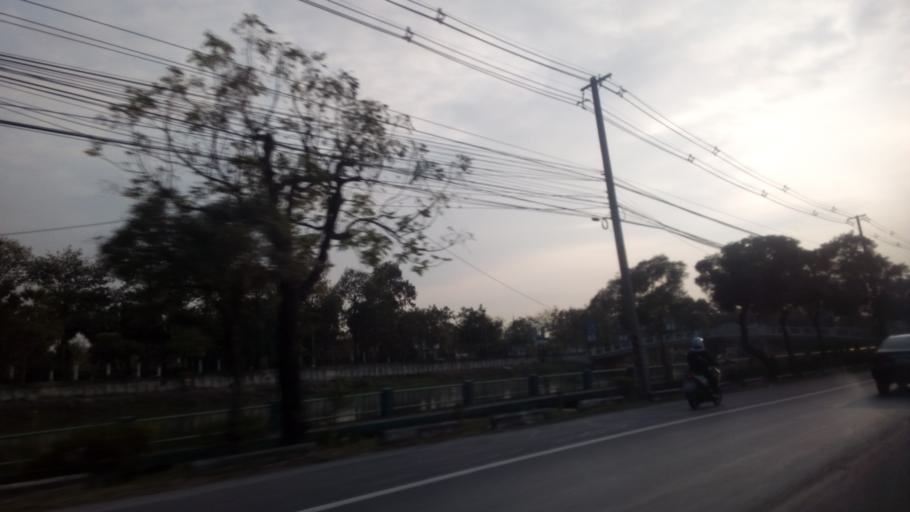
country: TH
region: Pathum Thani
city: Thanyaburi
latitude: 14.0049
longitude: 100.6987
